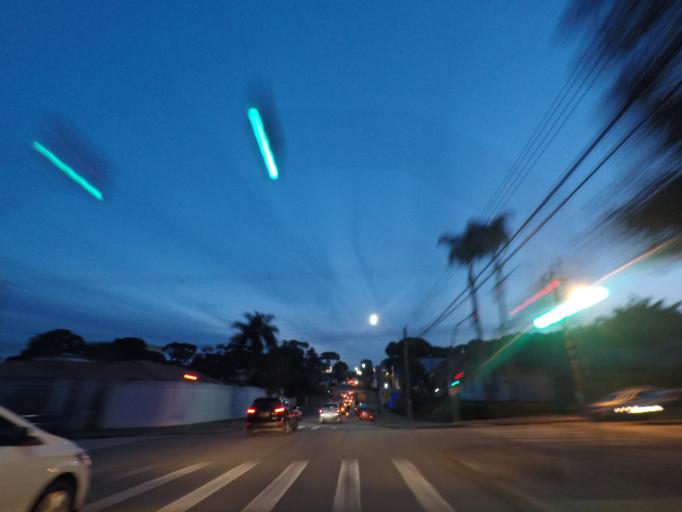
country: BR
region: Parana
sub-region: Curitiba
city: Curitiba
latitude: -25.4392
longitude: -49.2956
